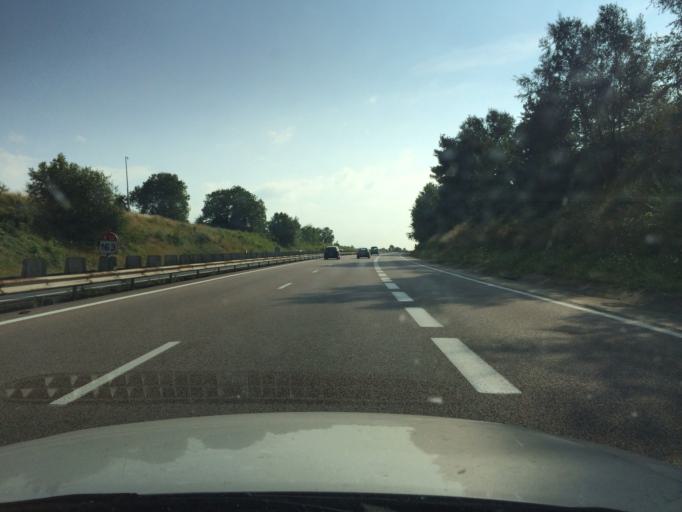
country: FR
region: Haute-Normandie
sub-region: Departement de l'Eure
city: Toutainville
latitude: 49.3403
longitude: 0.4200
